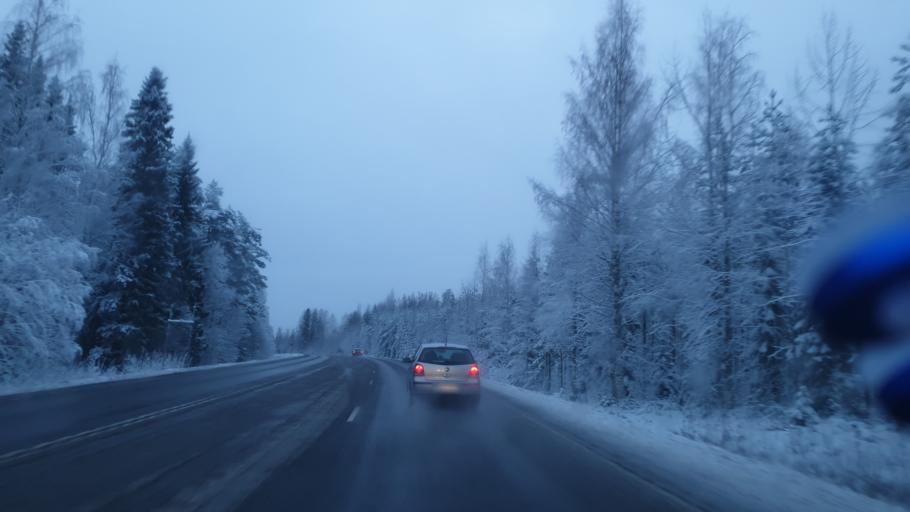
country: FI
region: Central Finland
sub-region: Saarijaervi-Viitasaari
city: Viitasaari
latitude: 63.0361
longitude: 25.8100
